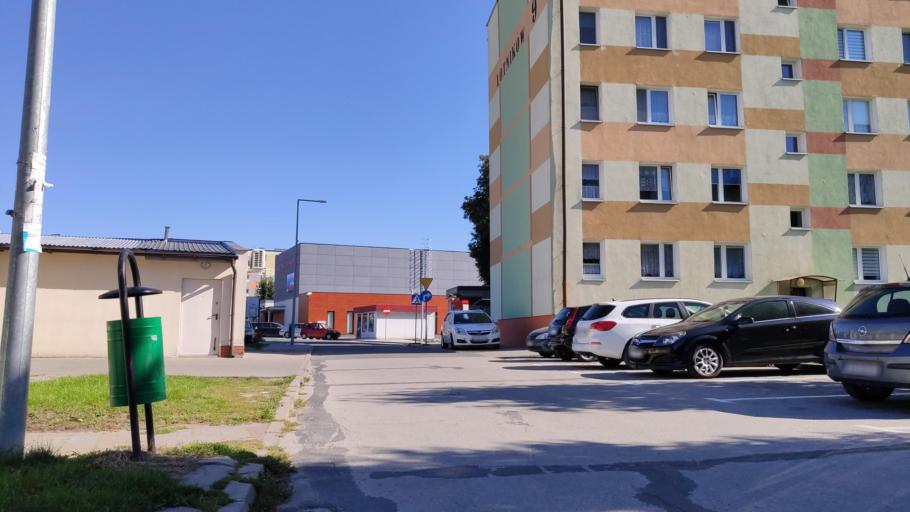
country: PL
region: Kujawsko-Pomorskie
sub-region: Powiat zninski
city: Barcin
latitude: 52.8545
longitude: 17.9406
